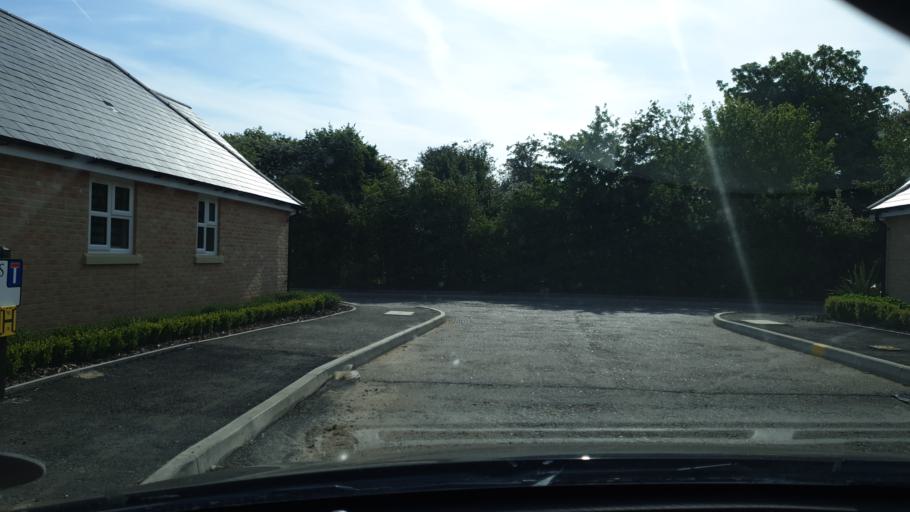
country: GB
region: England
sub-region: Essex
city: Frinton-on-Sea
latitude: 51.8427
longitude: 1.2244
